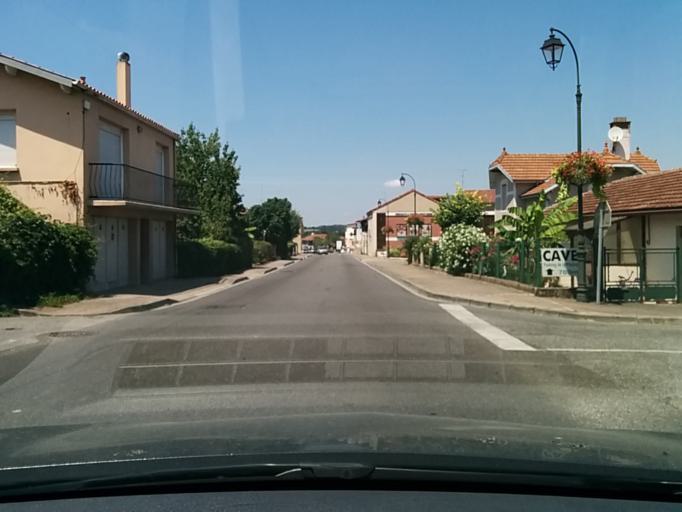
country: FR
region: Midi-Pyrenees
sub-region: Departement du Gers
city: Gimont
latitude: 43.6258
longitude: 0.8792
